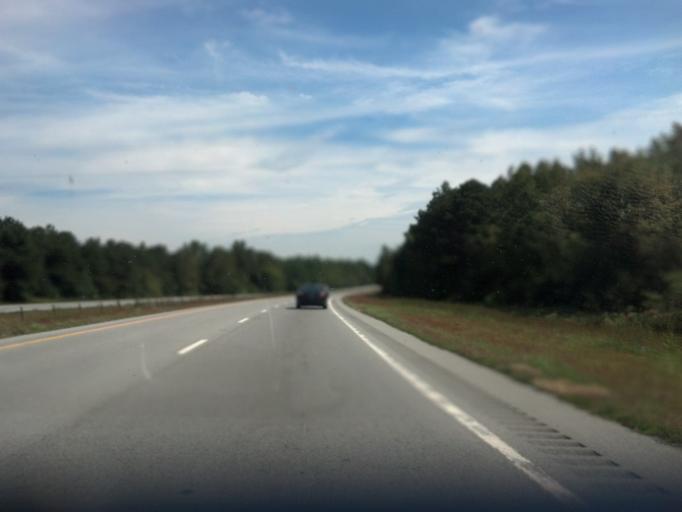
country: US
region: North Carolina
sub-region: Pitt County
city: Farmville
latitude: 35.6093
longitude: -77.5098
